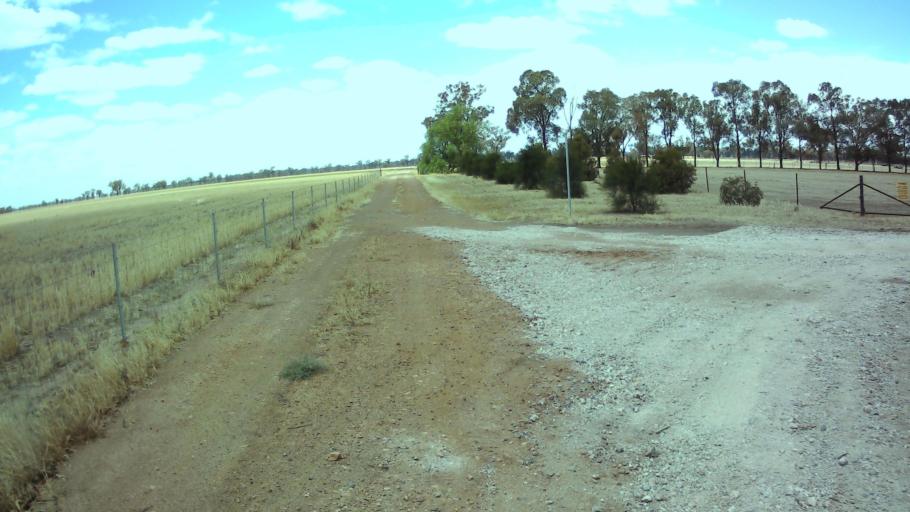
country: AU
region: New South Wales
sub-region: Weddin
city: Grenfell
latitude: -34.0531
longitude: 147.9424
